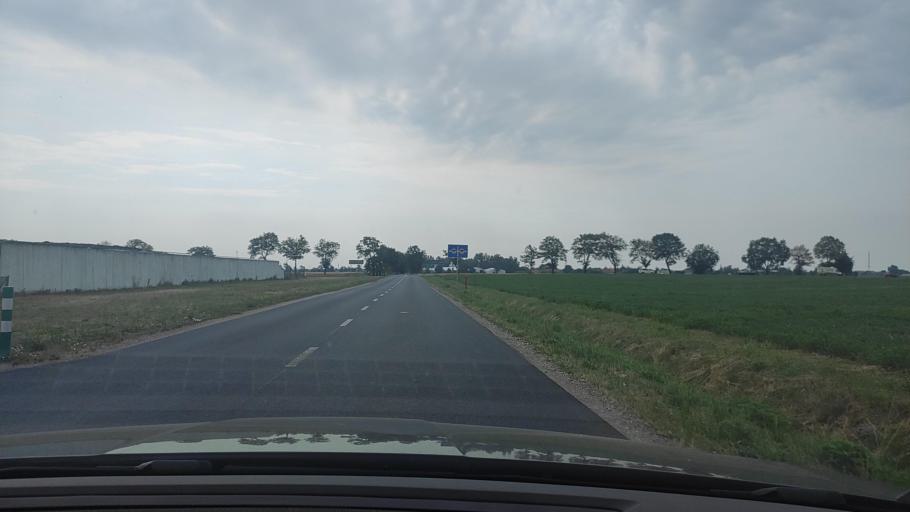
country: PL
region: Greater Poland Voivodeship
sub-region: Powiat poznanski
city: Kornik
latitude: 52.2903
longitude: 17.1124
